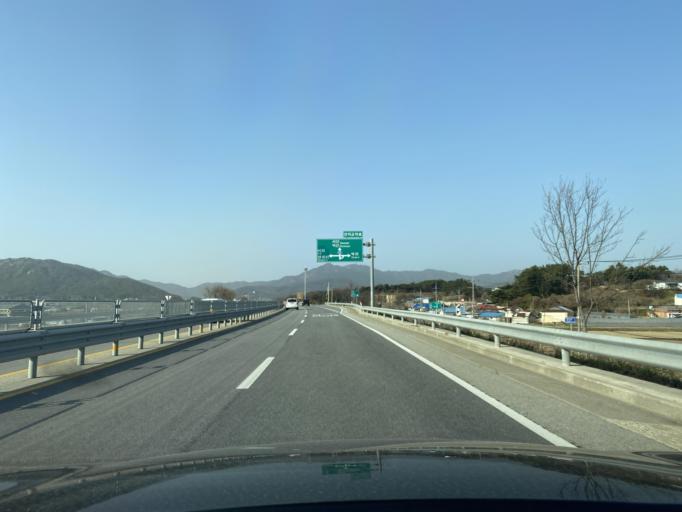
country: KR
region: Chungcheongnam-do
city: Hongsung
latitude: 36.6910
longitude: 126.6996
